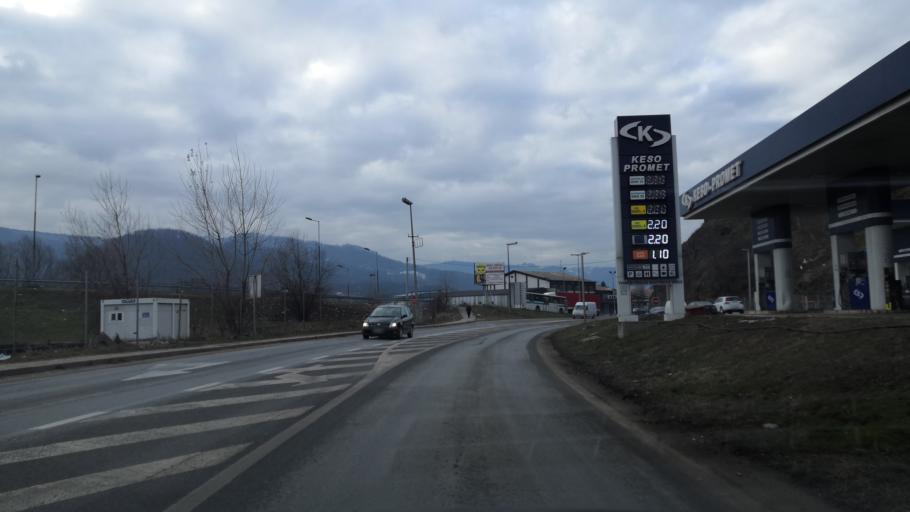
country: BA
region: Republika Srpska
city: Zvornik
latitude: 44.4074
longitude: 19.1236
